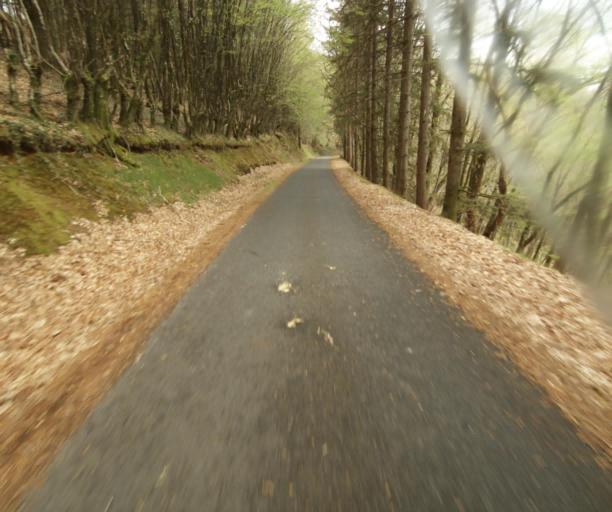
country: FR
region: Limousin
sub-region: Departement de la Correze
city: Naves
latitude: 45.3047
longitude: 1.8083
